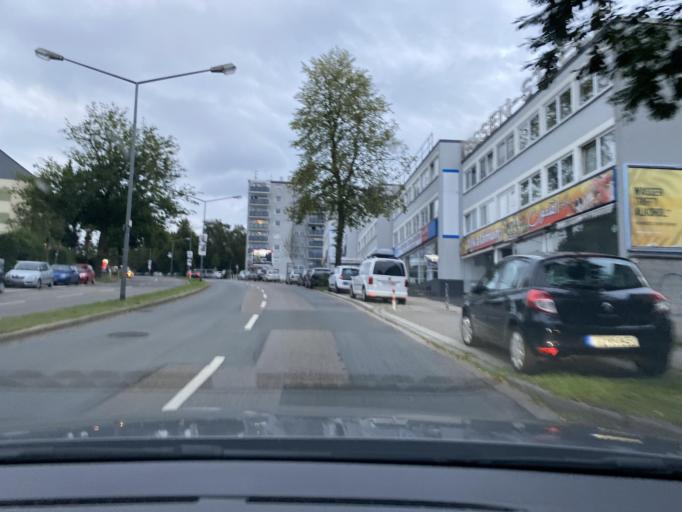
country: DE
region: North Rhine-Westphalia
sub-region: Regierungsbezirk Munster
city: Gelsenkirchen
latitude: 51.4451
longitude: 7.0914
